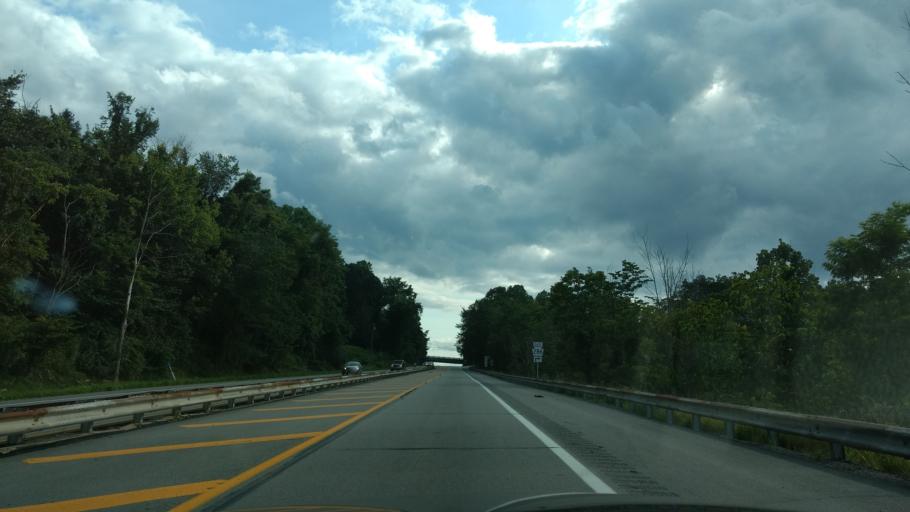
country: US
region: Pennsylvania
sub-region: Allegheny County
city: Plum
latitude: 40.4933
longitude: -79.6901
